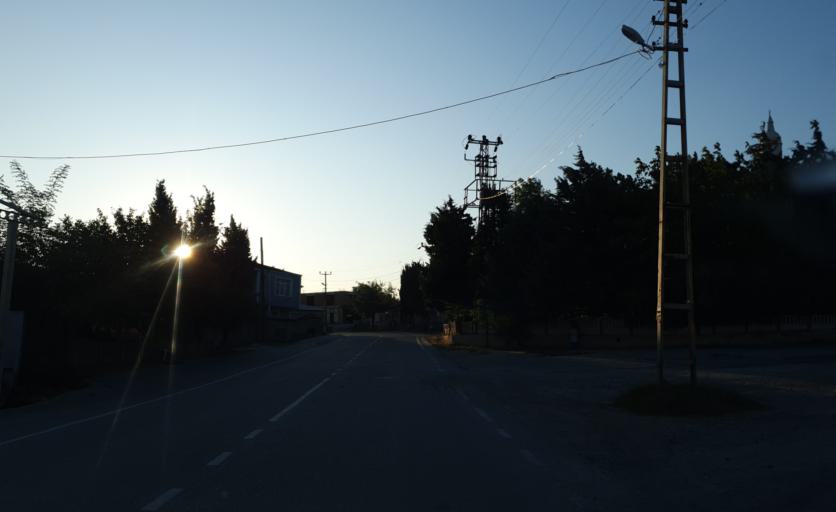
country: TR
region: Tekirdag
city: Beyazkoy
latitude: 41.3361
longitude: 27.7371
